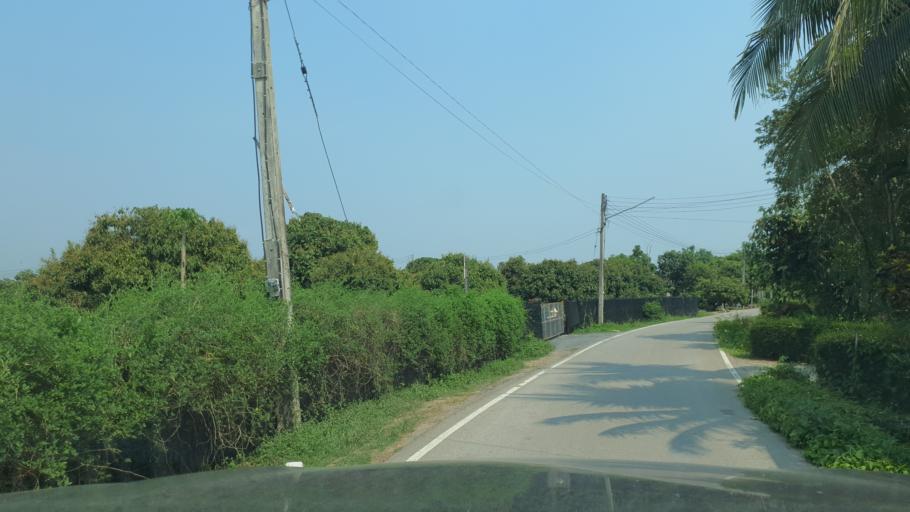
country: TH
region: Lamphun
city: Lamphun
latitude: 18.6519
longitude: 98.9878
